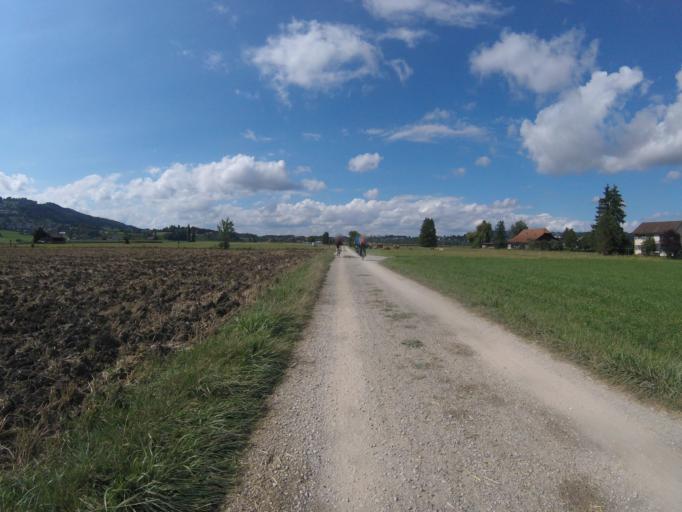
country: CH
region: Bern
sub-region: Bern-Mittelland District
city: Belp
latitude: 46.9082
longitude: 7.4898
